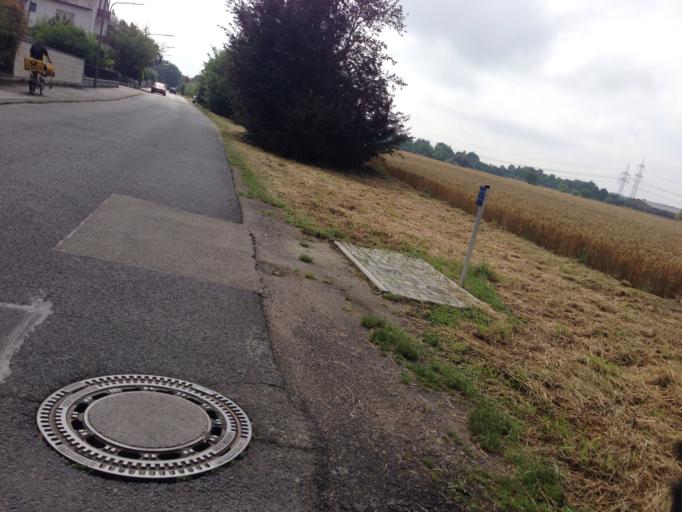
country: DE
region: Hesse
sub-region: Regierungsbezirk Darmstadt
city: Hanau am Main
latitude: 50.0968
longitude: 8.9209
